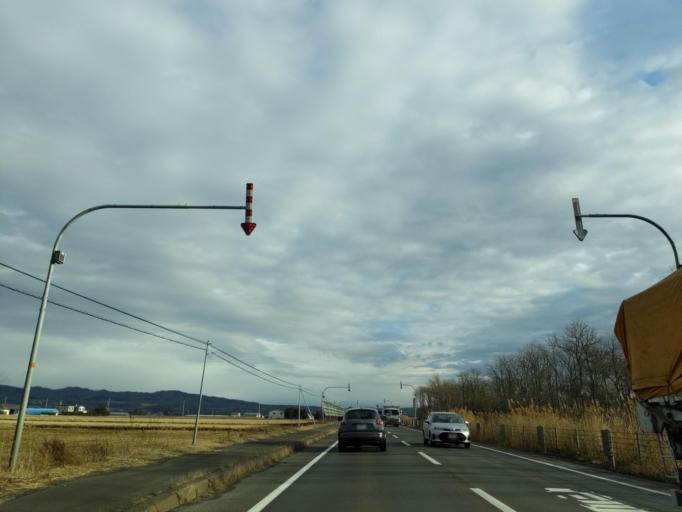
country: JP
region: Hokkaido
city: Kitahiroshima
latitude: 42.9620
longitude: 141.6850
